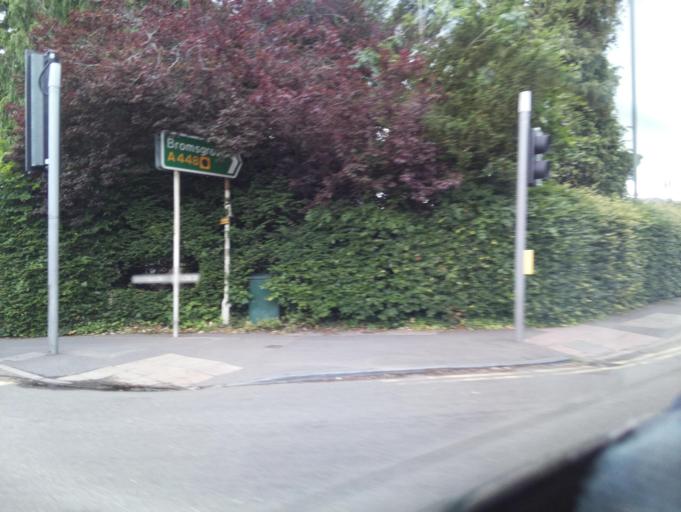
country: GB
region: England
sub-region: Worcestershire
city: Kidderminster
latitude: 52.3844
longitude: -2.2347
